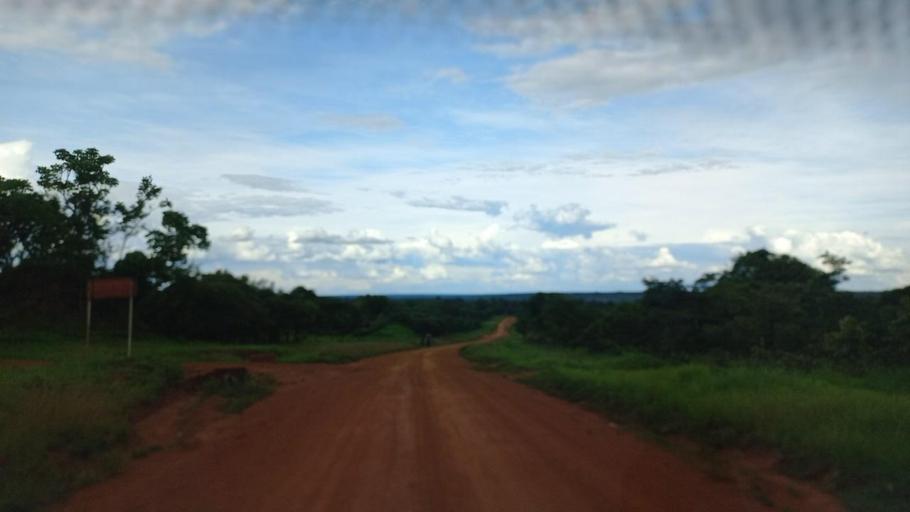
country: ZM
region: North-Western
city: Mwinilunga
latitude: -11.7623
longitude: 24.4154
